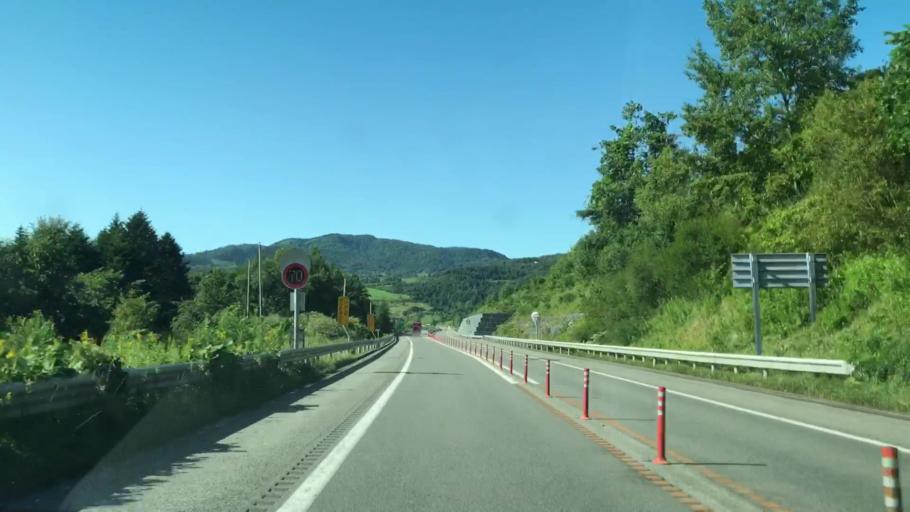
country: JP
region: Hokkaido
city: Date
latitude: 42.5402
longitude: 140.7955
